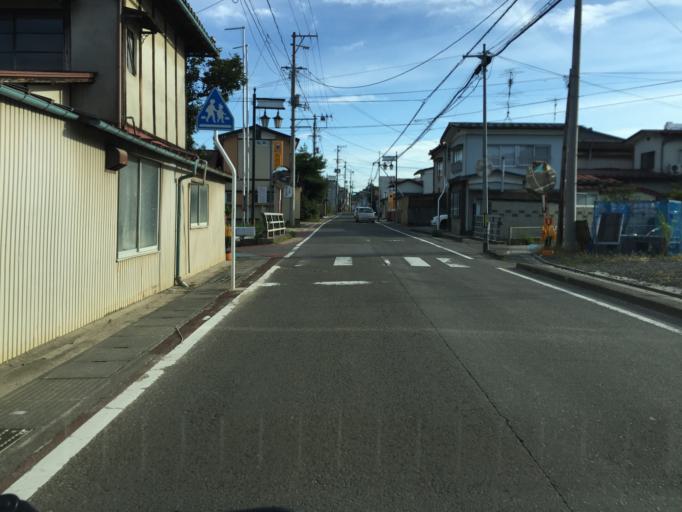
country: JP
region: Fukushima
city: Hobaramachi
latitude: 37.7869
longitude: 140.5944
